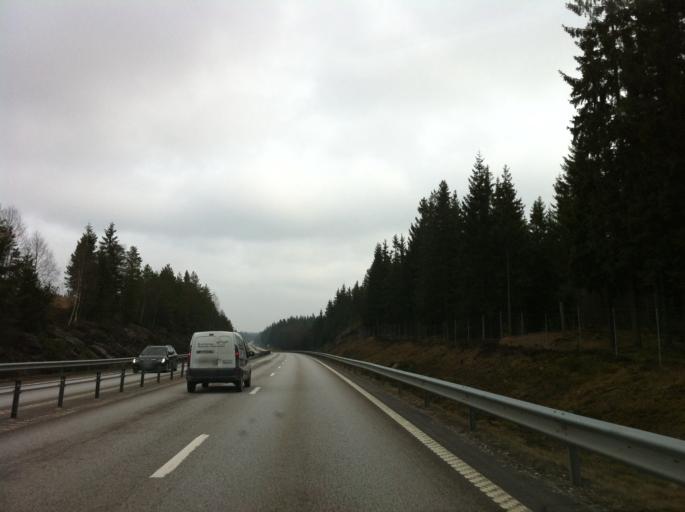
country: SE
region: Vaestra Goetaland
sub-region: Boras Kommun
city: Dalsjofors
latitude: 57.7525
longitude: 13.1080
